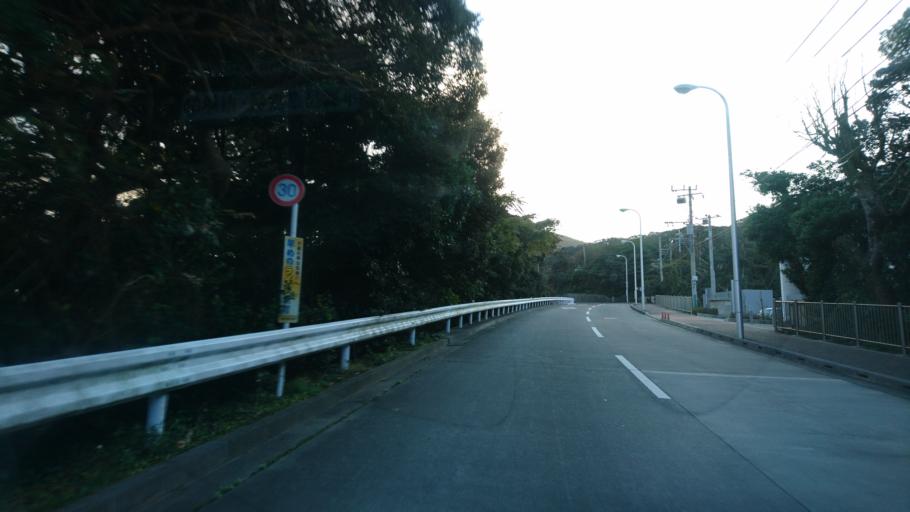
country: JP
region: Shizuoka
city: Shimoda
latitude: 34.3687
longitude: 139.2590
